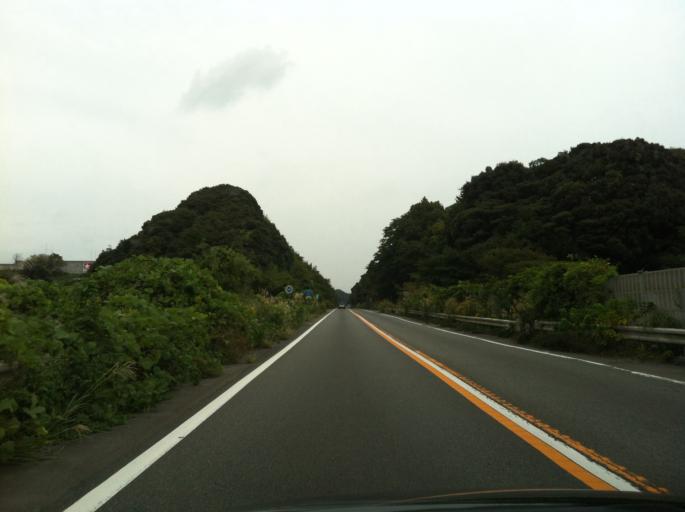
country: JP
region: Shizuoka
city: Kakegawa
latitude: 34.7841
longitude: 138.0371
